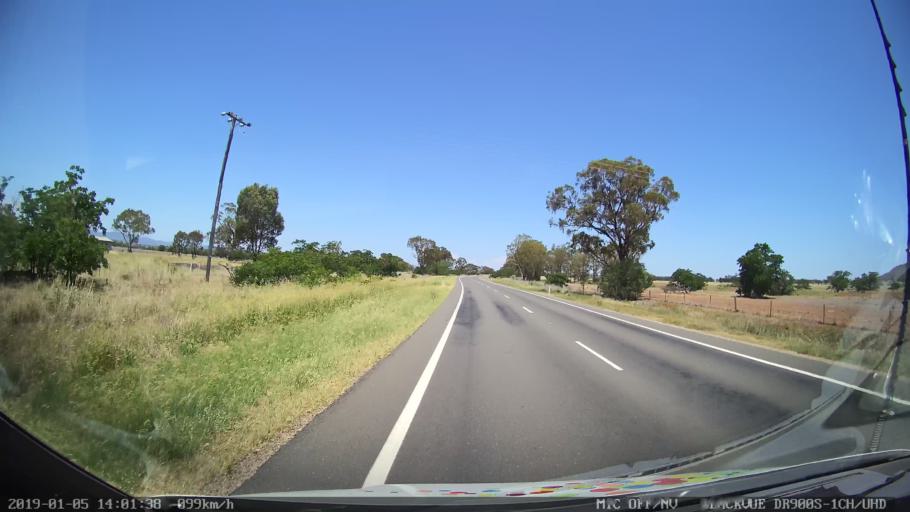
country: AU
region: New South Wales
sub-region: Gunnedah
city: Gunnedah
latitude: -31.1718
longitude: 150.3275
